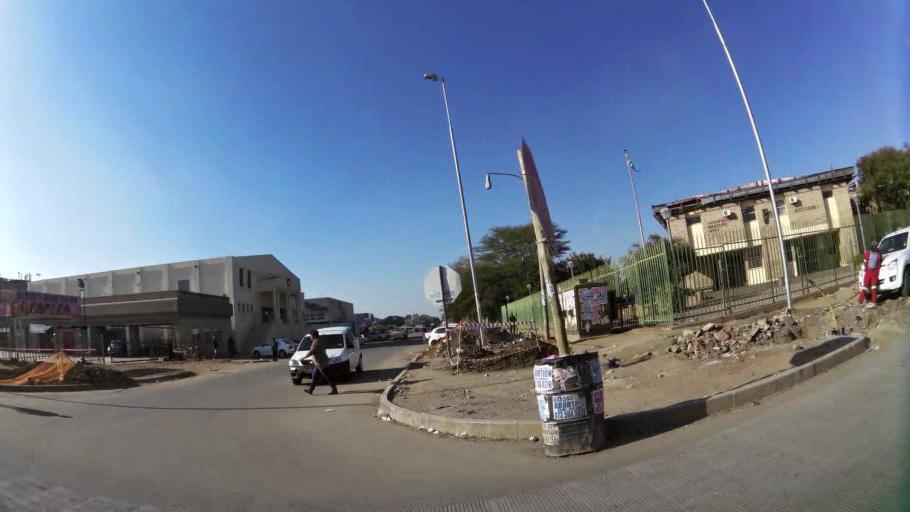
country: ZA
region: North-West
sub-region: Bojanala Platinum District Municipality
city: Rustenburg
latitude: -25.6657
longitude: 27.2364
